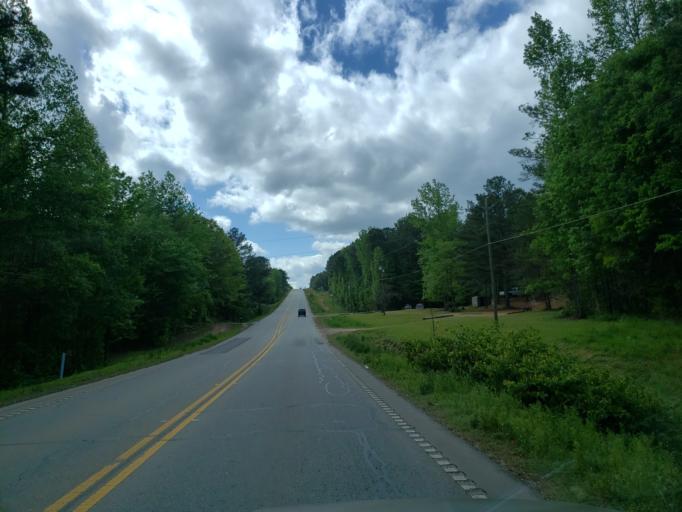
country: US
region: Georgia
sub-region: Haralson County
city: Bremen
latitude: 33.7107
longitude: -85.2071
